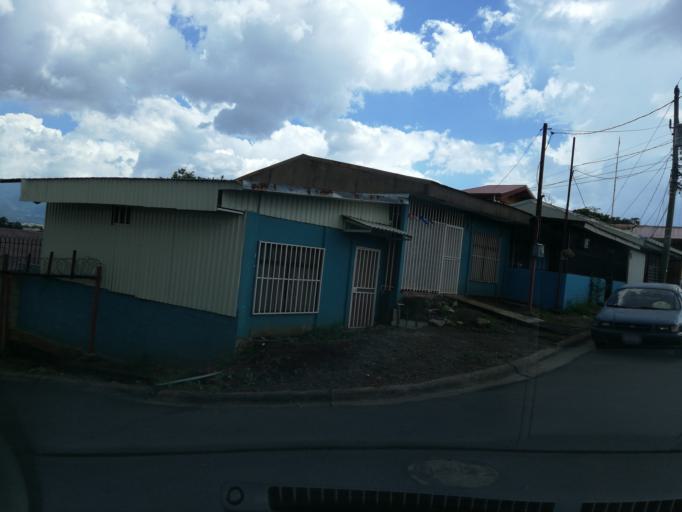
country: CR
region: Alajuela
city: Alajuela
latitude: 10.0163
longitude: -84.2025
